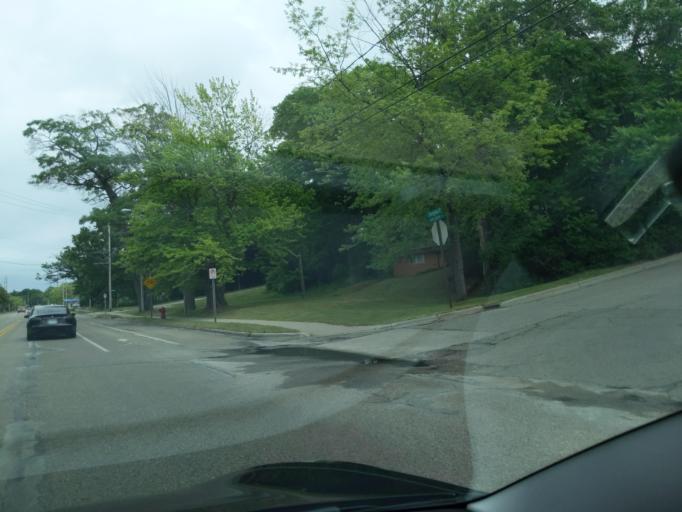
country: US
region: Michigan
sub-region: Muskegon County
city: Roosevelt Park
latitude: 43.2141
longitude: -86.3070
